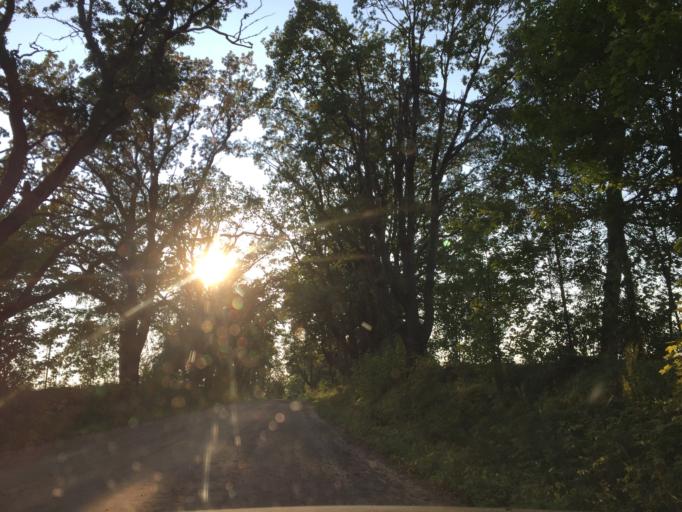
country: LV
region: Limbazu Rajons
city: Limbazi
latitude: 57.5504
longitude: 24.7890
